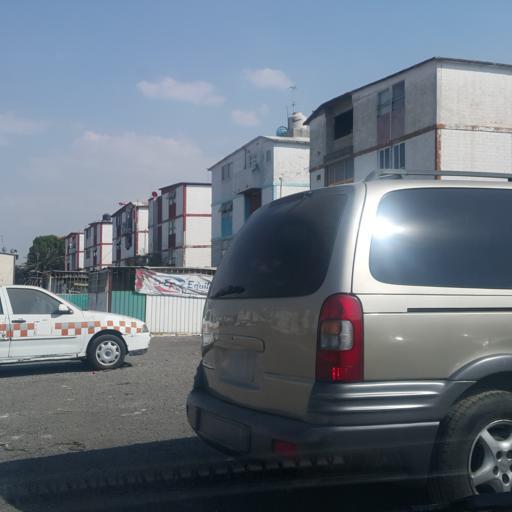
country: MX
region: Mexico
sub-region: Jaltenco
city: Alborada Jaltenco
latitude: 19.6605
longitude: -99.0693
